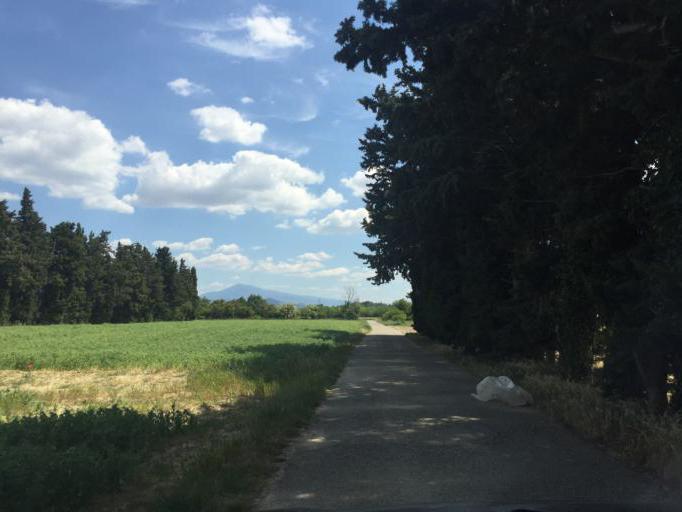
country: FR
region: Provence-Alpes-Cote d'Azur
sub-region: Departement du Vaucluse
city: Jonquieres
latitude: 44.1202
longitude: 4.9201
